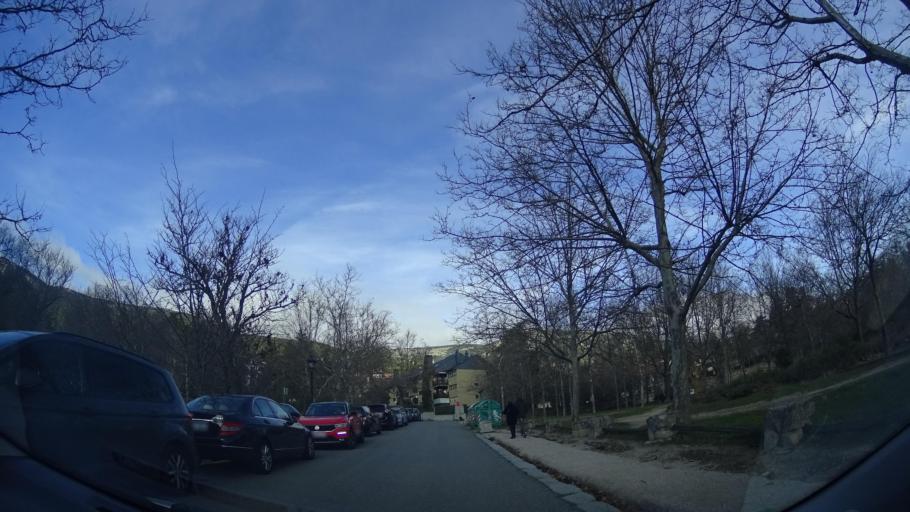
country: ES
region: Madrid
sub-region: Provincia de Madrid
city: San Lorenzo de El Escorial
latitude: 40.5864
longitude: -4.1545
